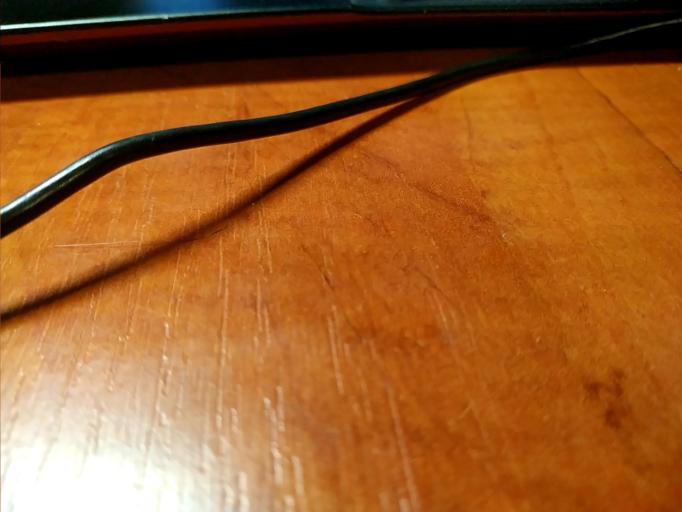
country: RU
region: Moscow
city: Rostokino
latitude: 55.8341
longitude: 37.6794
